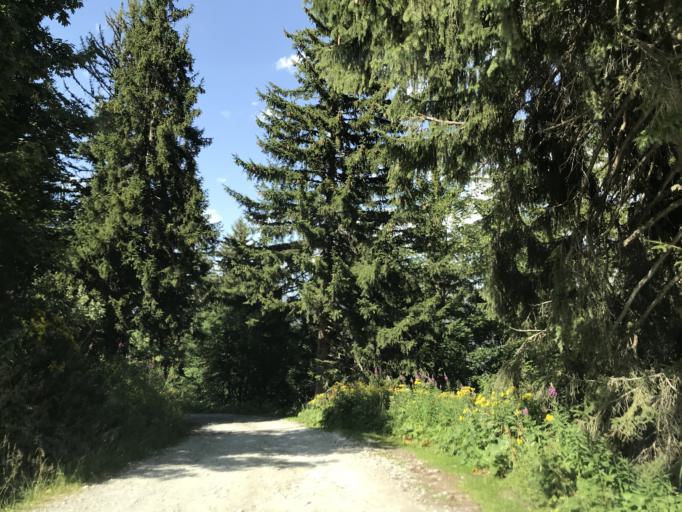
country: FR
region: Rhone-Alpes
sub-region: Departement de la Savoie
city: Beaufort
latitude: 45.6810
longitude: 6.6114
